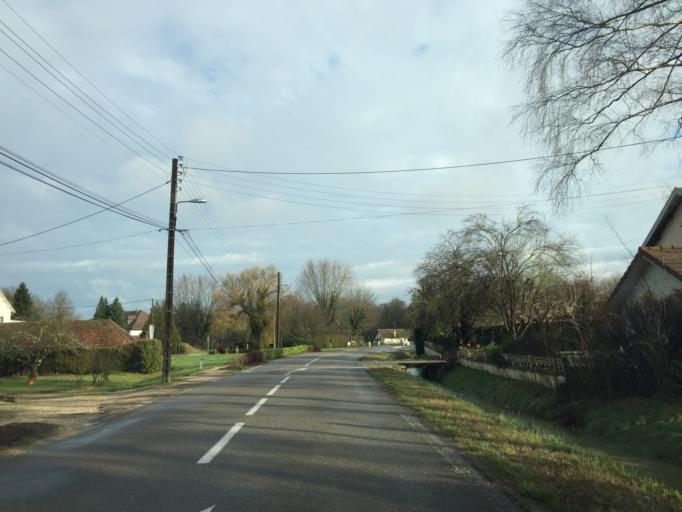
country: FR
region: Franche-Comte
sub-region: Departement du Jura
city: Mont-sous-Vaudrey
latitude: 46.9816
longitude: 5.5975
